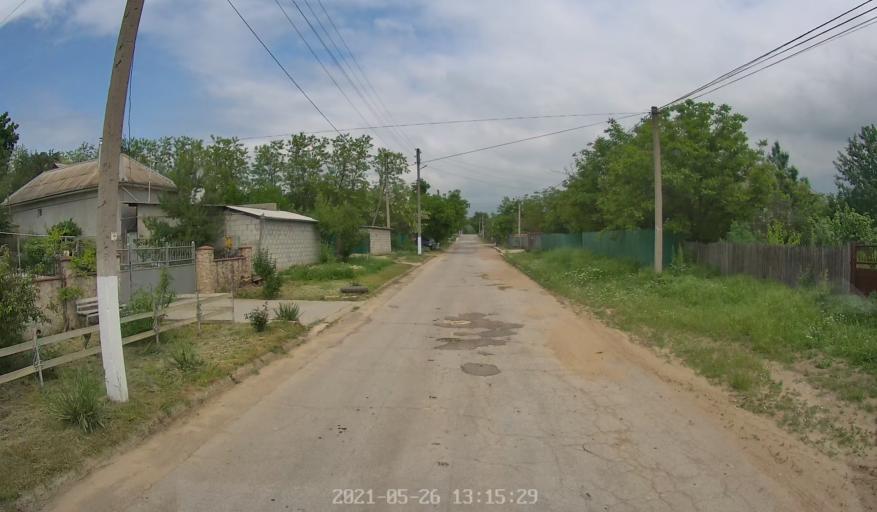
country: MD
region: Hincesti
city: Dancu
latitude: 46.7602
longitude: 28.3415
